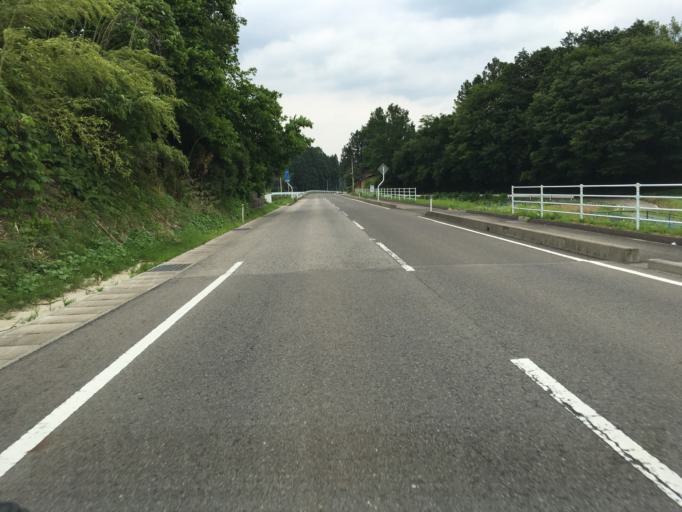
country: JP
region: Fukushima
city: Nihommatsu
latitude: 37.6398
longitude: 140.5357
